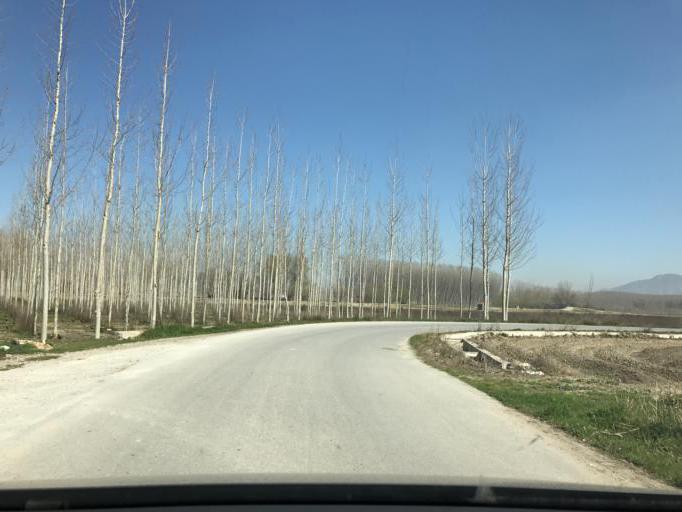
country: ES
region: Andalusia
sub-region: Provincia de Granada
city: Cijuela
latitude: 37.2088
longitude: -3.8069
